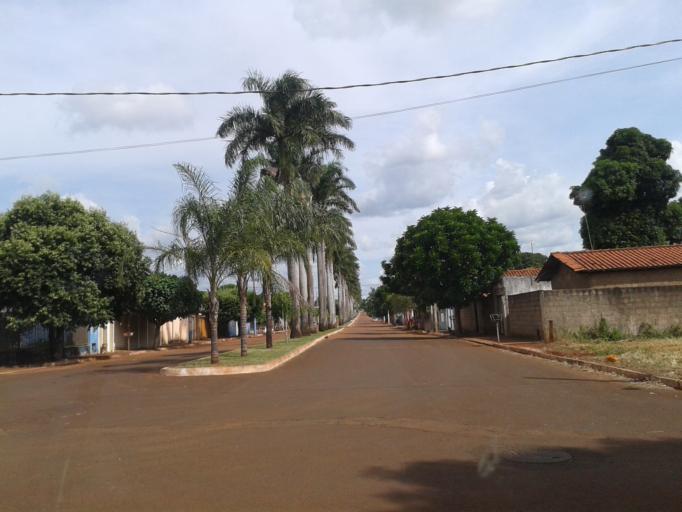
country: BR
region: Minas Gerais
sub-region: Centralina
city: Centralina
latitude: -18.5804
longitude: -49.1955
